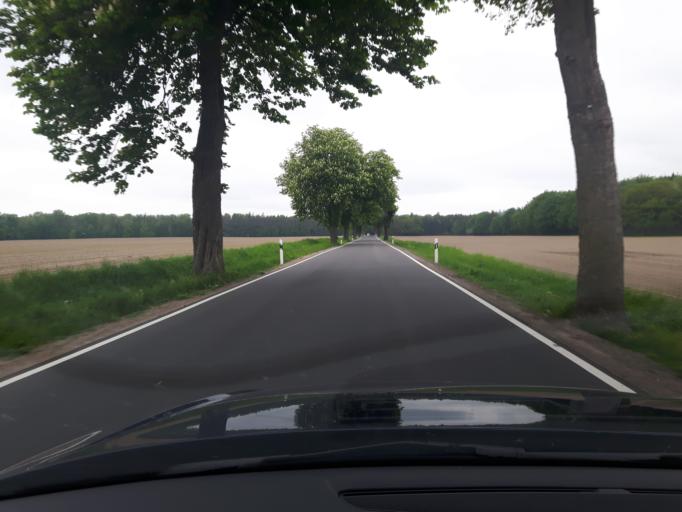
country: DE
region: Mecklenburg-Vorpommern
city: Gnoien
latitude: 53.9957
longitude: 12.6805
